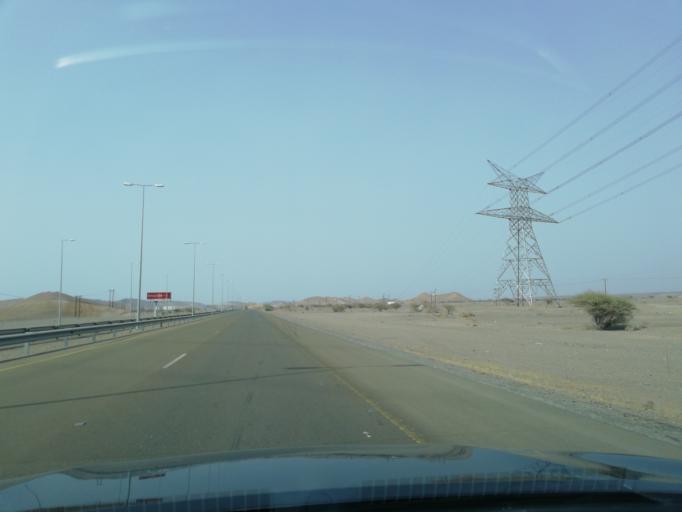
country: OM
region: Al Batinah
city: Al Liwa'
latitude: 24.3565
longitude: 56.5259
